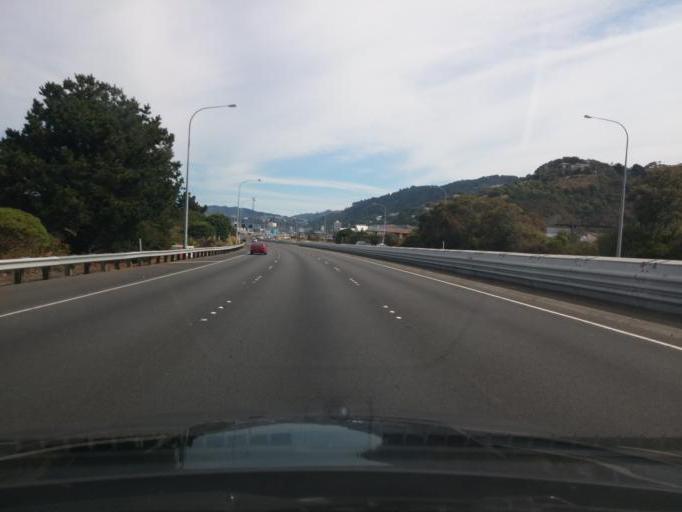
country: NZ
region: Wellington
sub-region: Wellington City
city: Wellington
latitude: -41.2583
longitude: 174.7941
